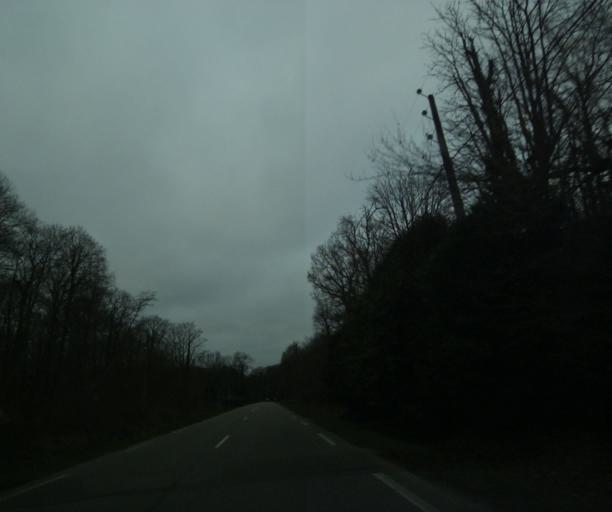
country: FR
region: Ile-de-France
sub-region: Departement des Yvelines
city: Chanteloup-les-Vignes
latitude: 48.9885
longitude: 2.0248
